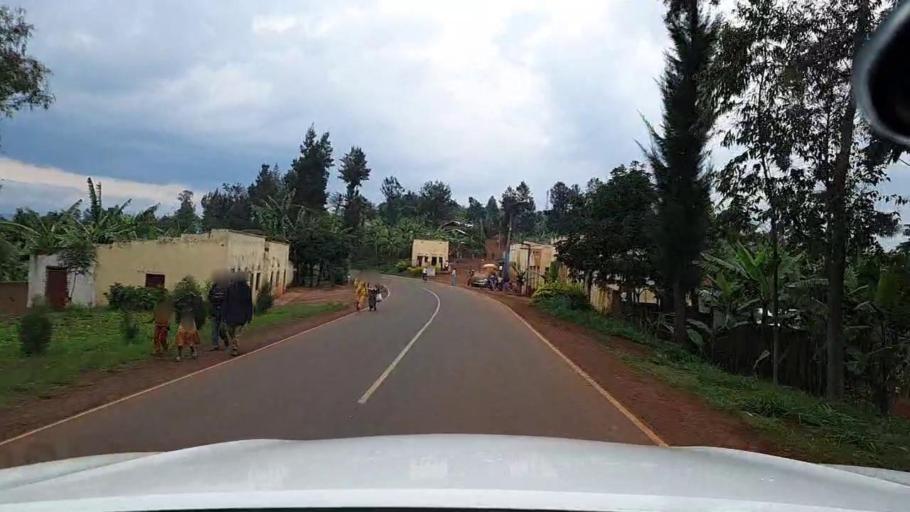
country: RW
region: Western Province
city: Cyangugu
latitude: -2.6455
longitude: 28.9579
